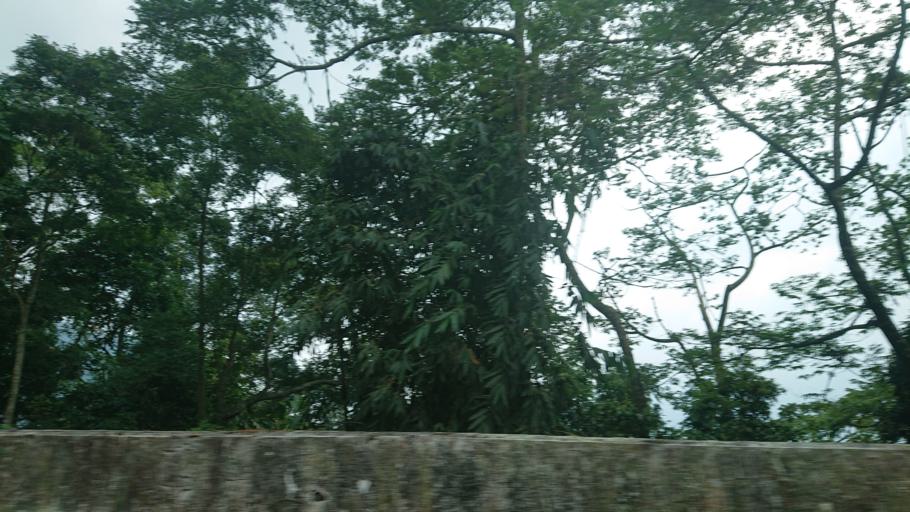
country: TW
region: Taiwan
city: Lugu
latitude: 23.5993
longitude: 120.7013
